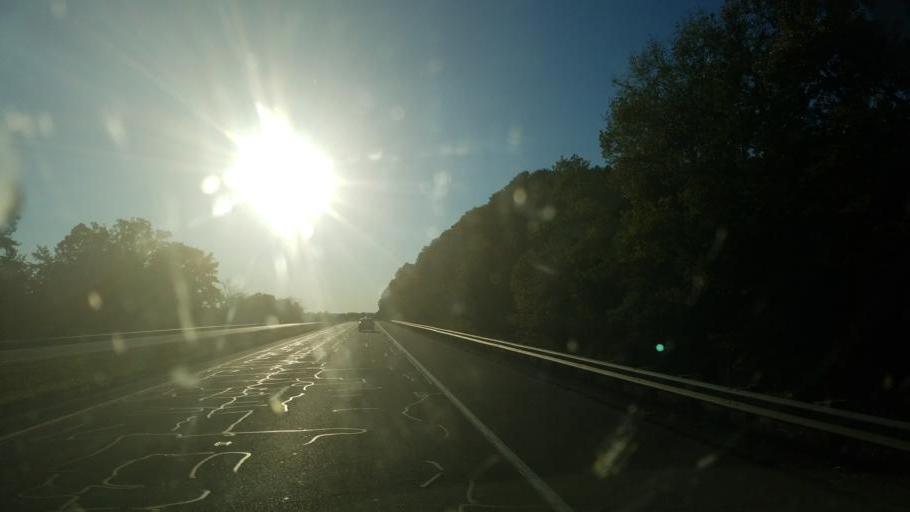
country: US
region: Ohio
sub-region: Tuscarawas County
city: Newcomerstown
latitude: 40.2828
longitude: -81.6453
